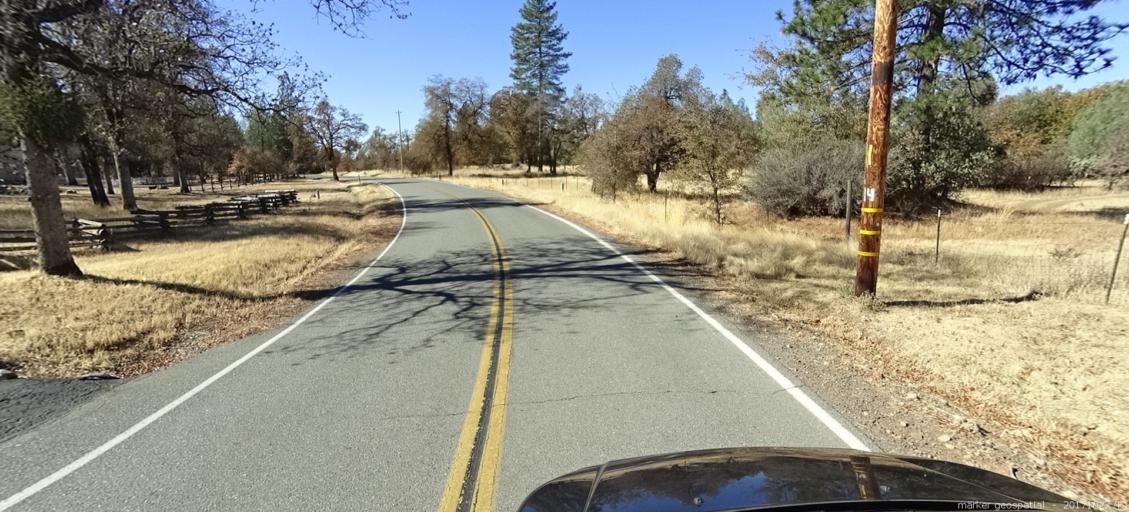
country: US
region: California
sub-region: Shasta County
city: Shingletown
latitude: 40.7552
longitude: -121.9749
